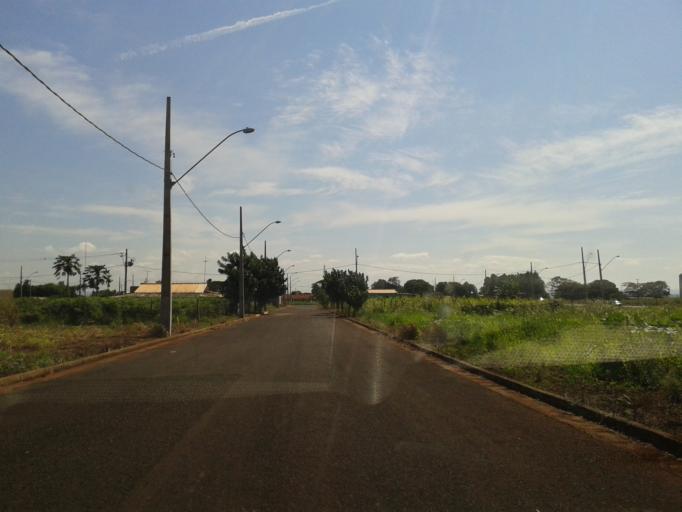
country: BR
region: Minas Gerais
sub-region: Centralina
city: Centralina
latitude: -18.5997
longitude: -49.1930
